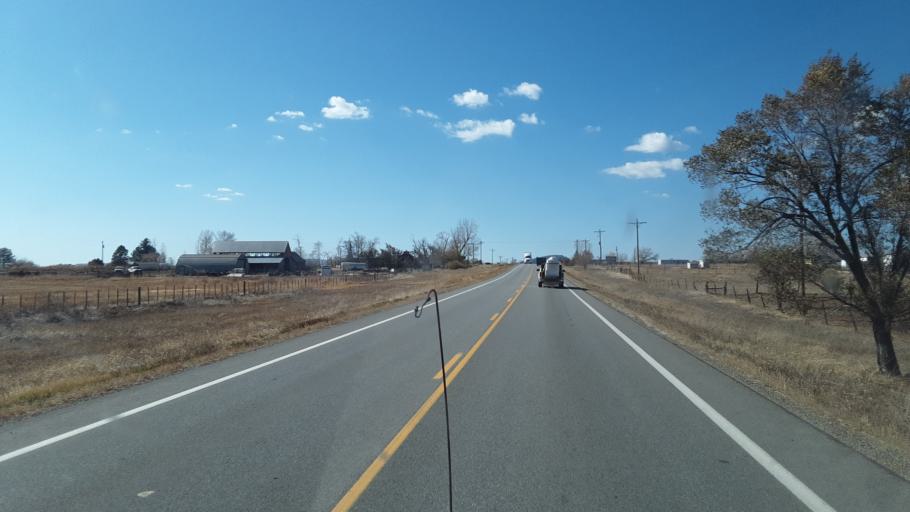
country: US
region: Colorado
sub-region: La Plata County
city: Durango
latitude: 37.2299
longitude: -107.7705
